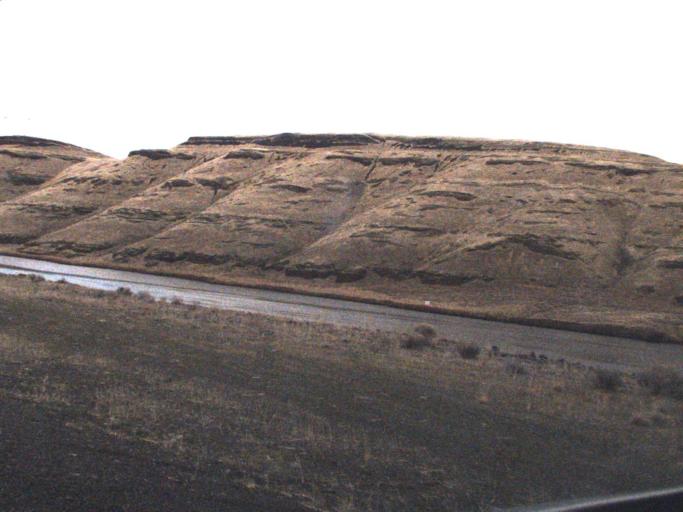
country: US
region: Washington
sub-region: Walla Walla County
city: Waitsburg
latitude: 46.5653
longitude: -118.1874
